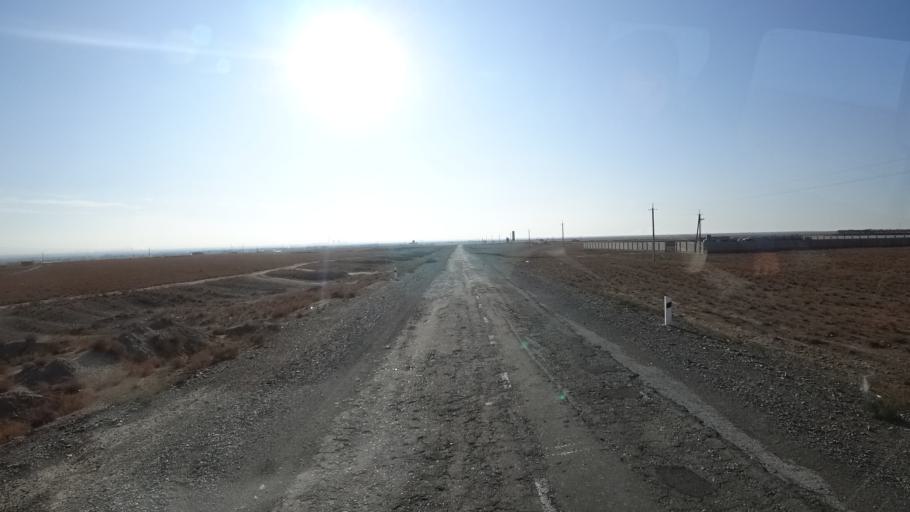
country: UZ
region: Navoiy
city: Beshrabot
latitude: 40.2257
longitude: 65.3987
